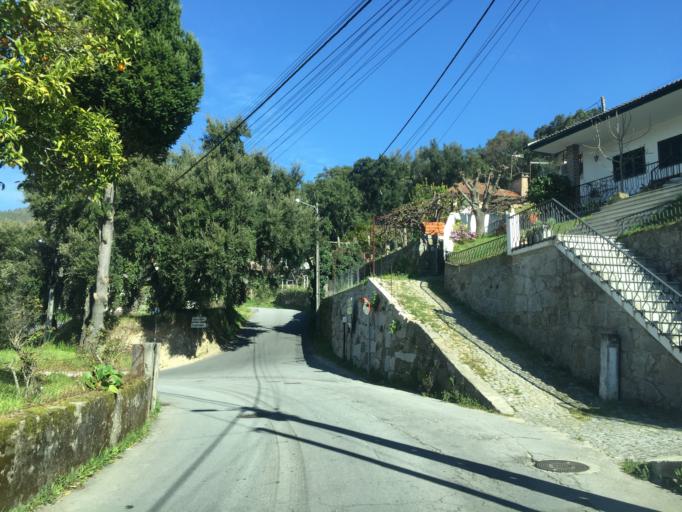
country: PT
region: Aveiro
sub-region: Arouca
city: Arouca
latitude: 40.9335
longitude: -8.2475
